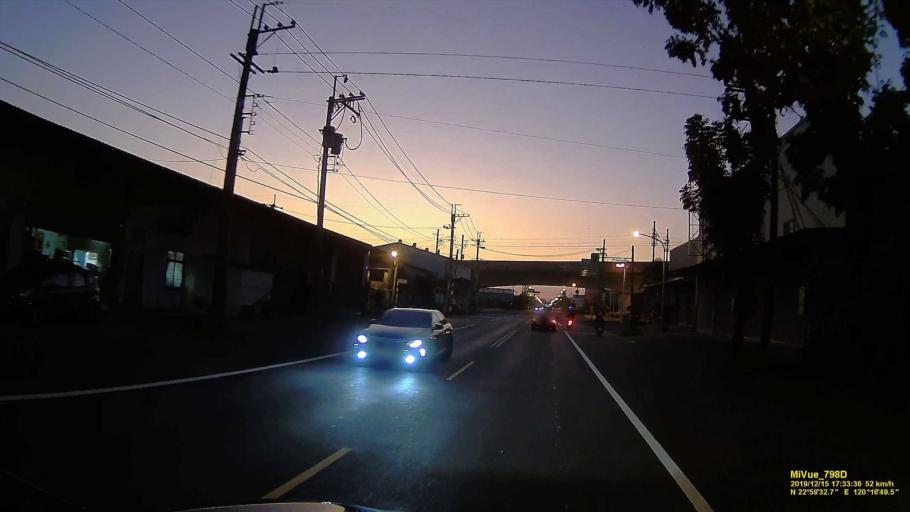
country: TW
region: Taiwan
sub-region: Tainan
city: Tainan
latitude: 22.9924
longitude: 120.2801
